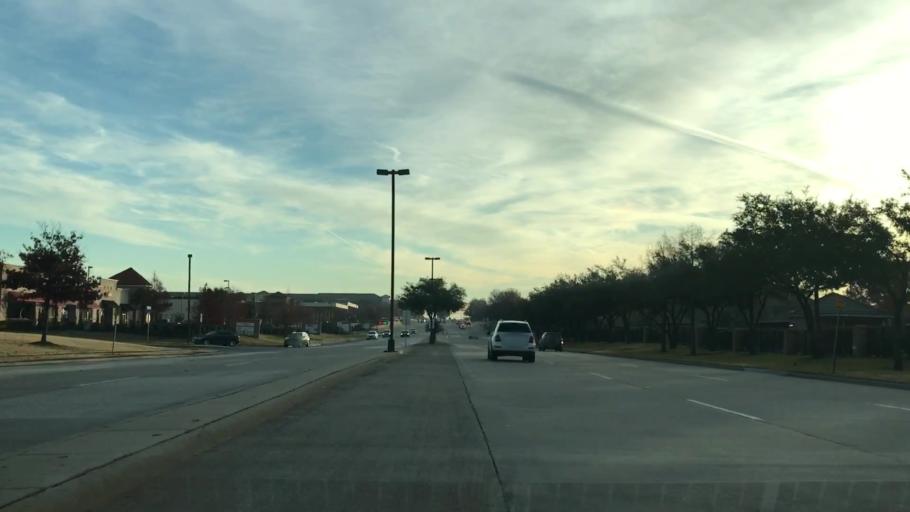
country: US
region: Texas
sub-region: Dallas County
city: Farmers Branch
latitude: 32.8959
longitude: -96.9633
